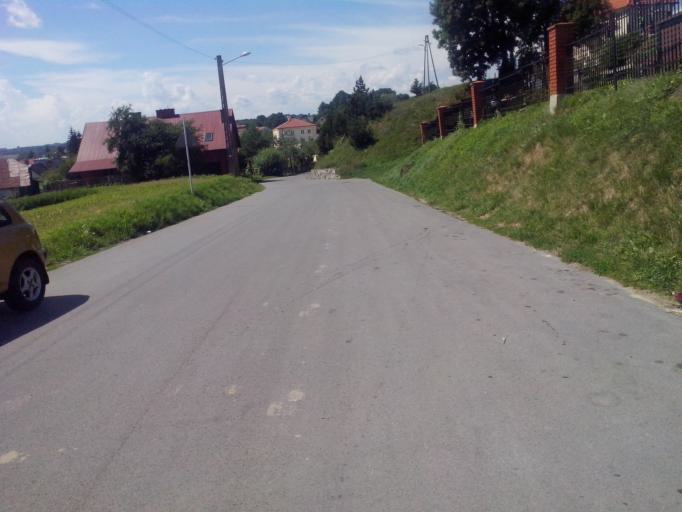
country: PL
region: Subcarpathian Voivodeship
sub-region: Powiat strzyzowski
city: Czudec
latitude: 49.9460
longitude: 21.8416
